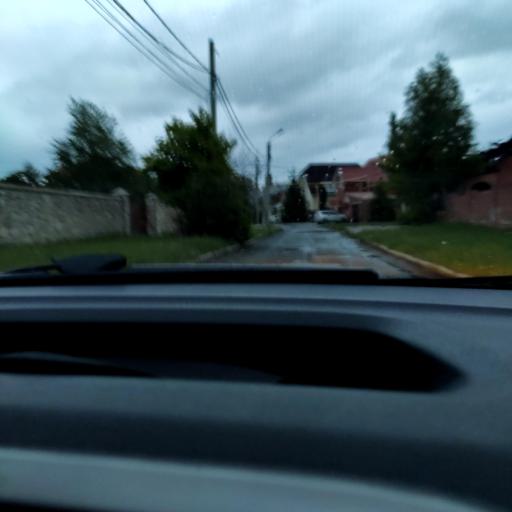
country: RU
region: Samara
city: Tol'yatti
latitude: 53.5416
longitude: 49.3752
